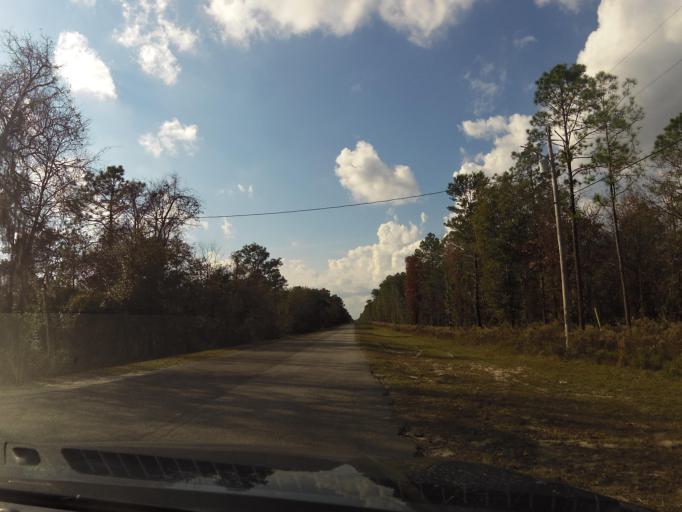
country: US
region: Florida
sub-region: Clay County
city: Middleburg
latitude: 30.1578
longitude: -81.9738
